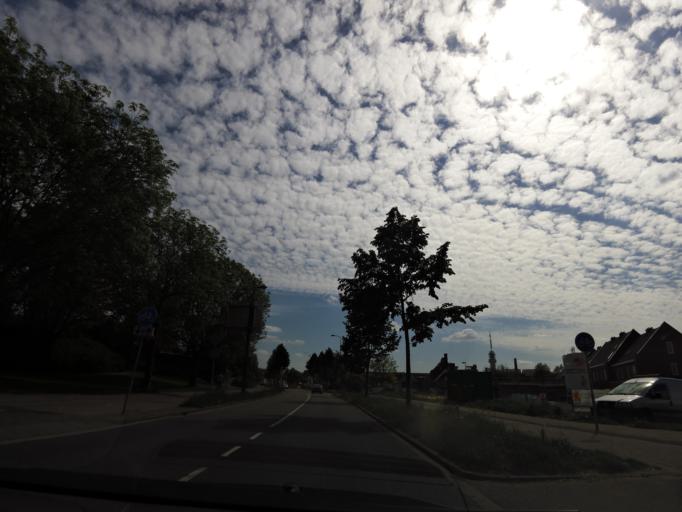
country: NL
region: Limburg
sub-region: Gemeente Roermond
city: Roermond
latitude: 51.1918
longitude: 5.9832
